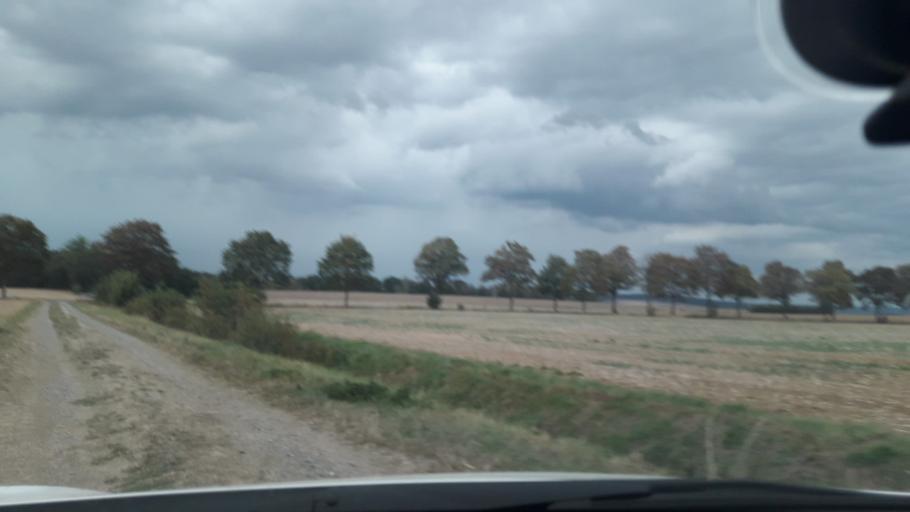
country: DE
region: Lower Saxony
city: Gielde
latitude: 52.0189
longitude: 10.4875
